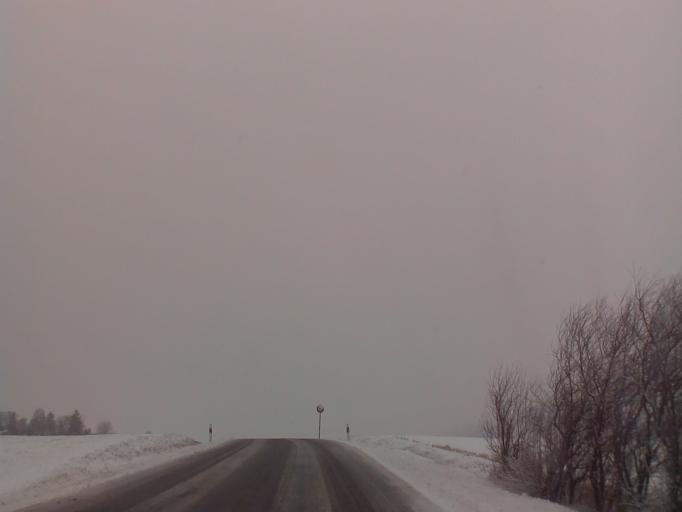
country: DE
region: Thuringia
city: Wandersleben
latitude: 50.8529
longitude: 10.8578
